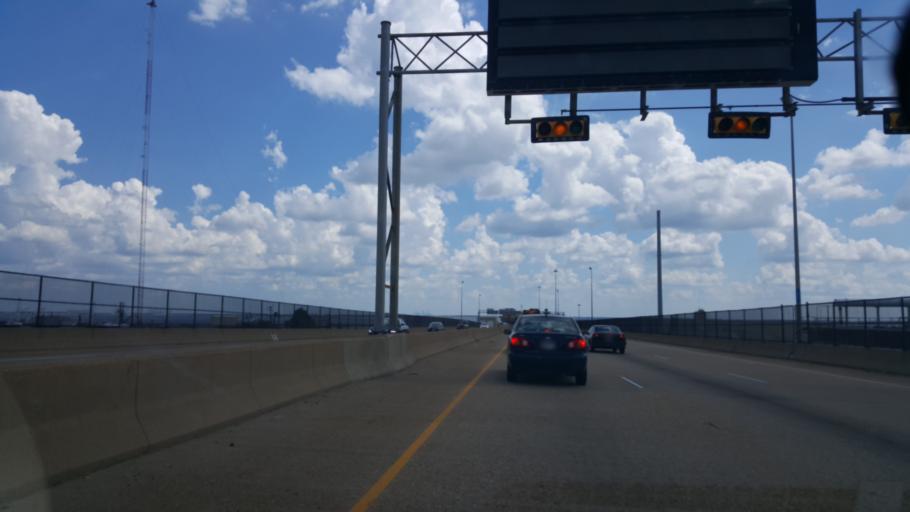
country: US
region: Virginia
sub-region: City of Newport News
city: Newport News
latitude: 36.9649
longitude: -76.4135
